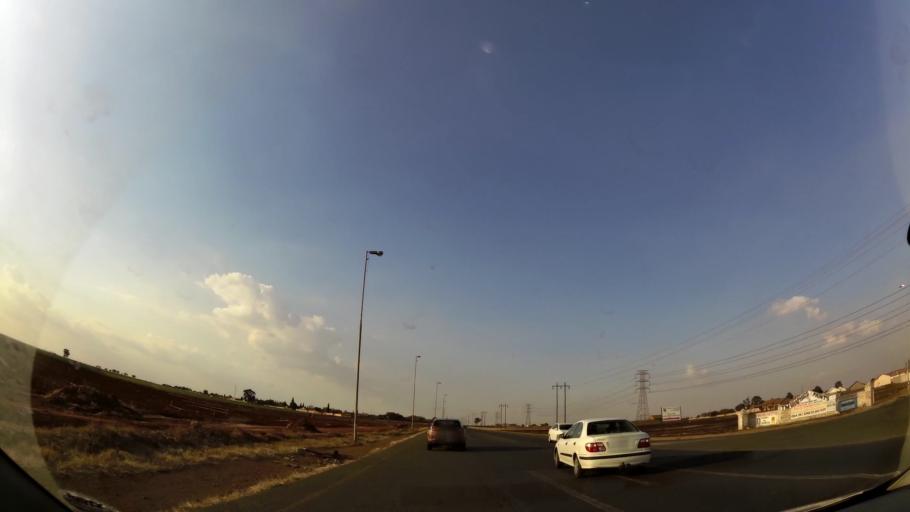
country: ZA
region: Gauteng
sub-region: Ekurhuleni Metropolitan Municipality
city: Germiston
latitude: -26.3230
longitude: 28.2443
